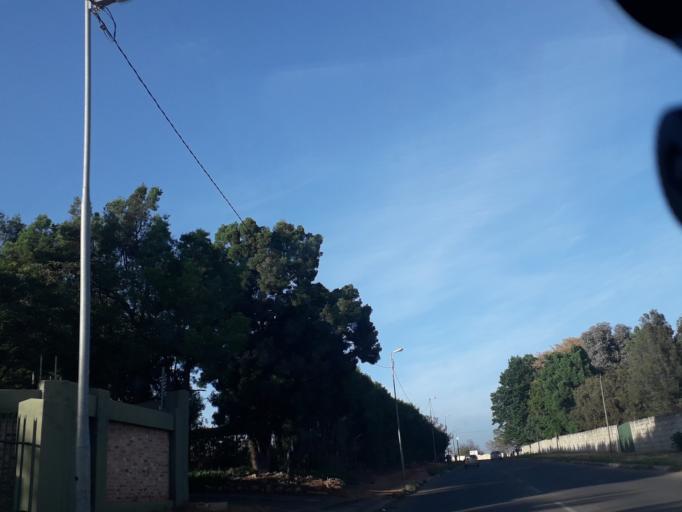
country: ZA
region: Gauteng
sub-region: City of Johannesburg Metropolitan Municipality
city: Roodepoort
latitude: -26.0910
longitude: 27.9017
